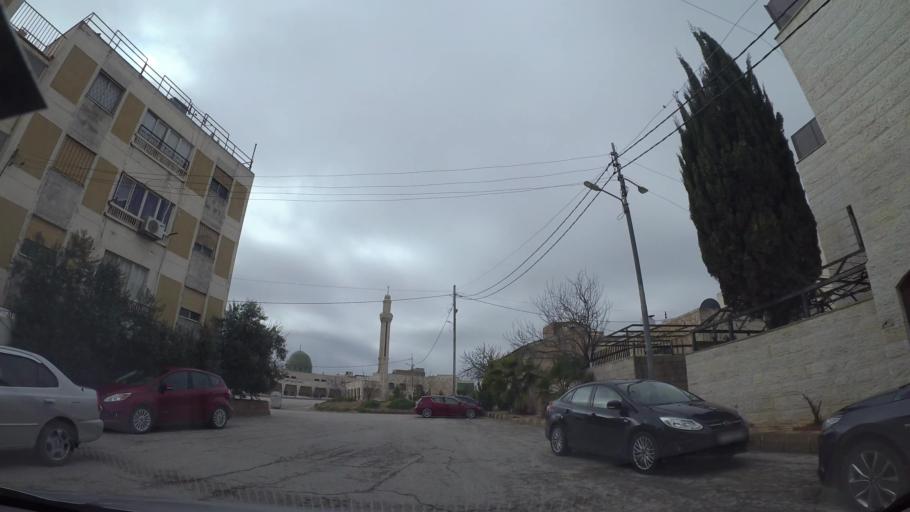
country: JO
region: Amman
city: Al Jubayhah
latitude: 32.0534
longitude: 35.8810
